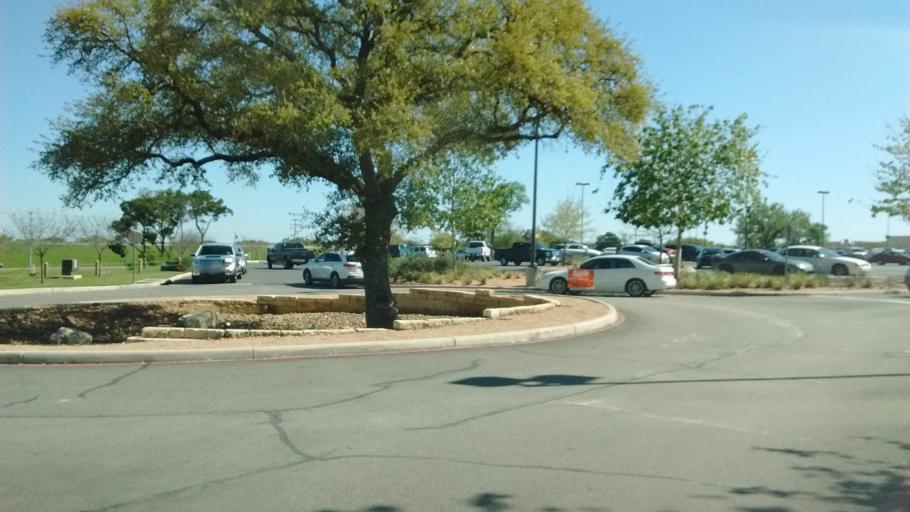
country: US
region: Texas
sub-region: Comal County
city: New Braunfels
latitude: 29.7149
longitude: -98.1599
